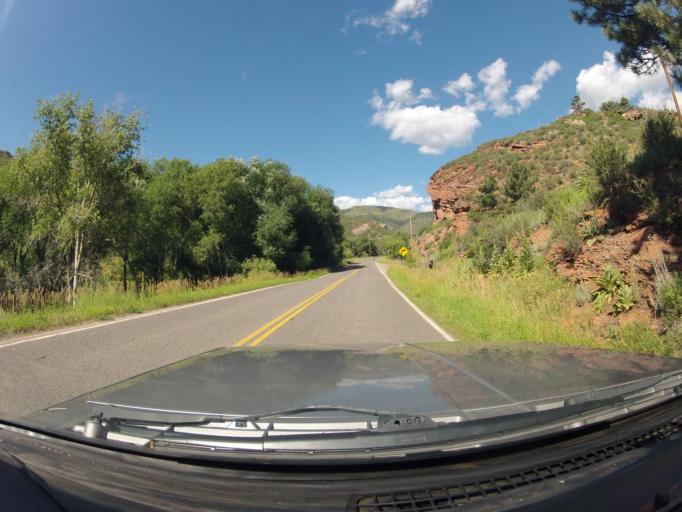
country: US
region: Colorado
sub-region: Larimer County
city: Laporte
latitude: 40.5045
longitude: -105.2339
